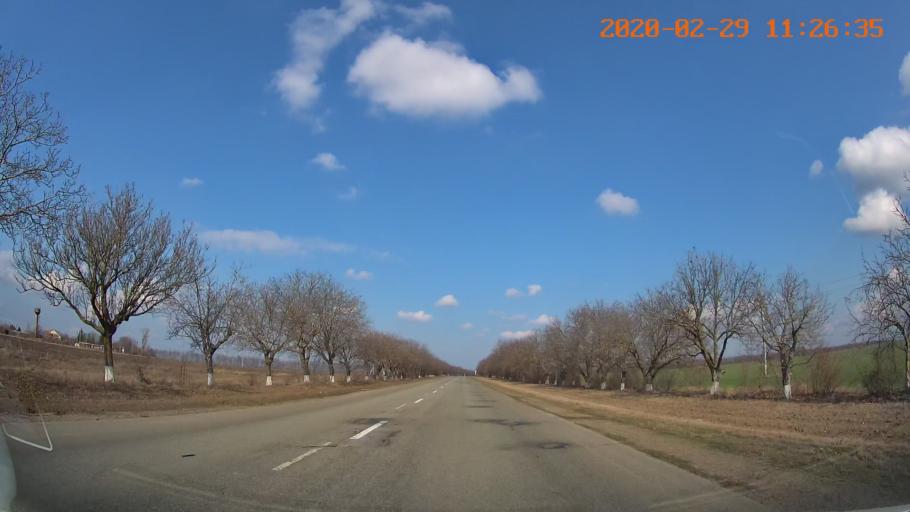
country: MD
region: Telenesti
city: Cocieri
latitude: 47.4551
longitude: 29.1455
